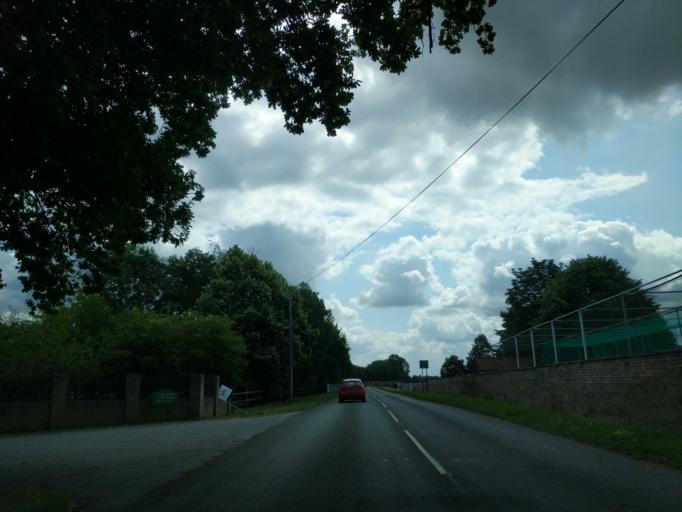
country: GB
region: England
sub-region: Cambridgeshire
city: Isleham
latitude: 52.2994
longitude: 0.4429
